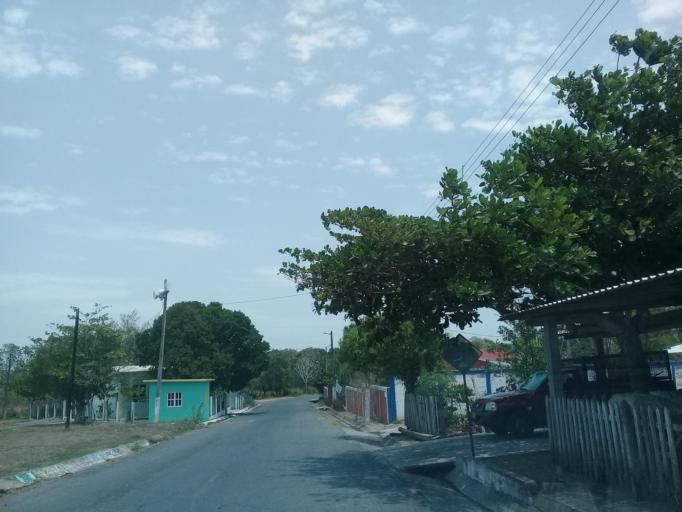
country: MX
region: Veracruz
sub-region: Veracruz
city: Delfino Victoria (Santa Fe)
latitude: 19.1713
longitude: -96.2974
